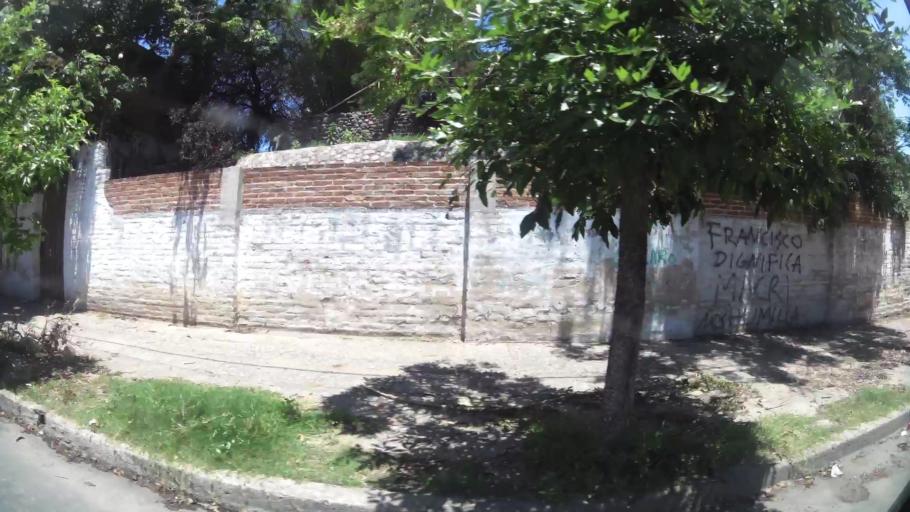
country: AR
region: Cordoba
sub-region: Departamento de Capital
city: Cordoba
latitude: -31.4006
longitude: -64.2223
